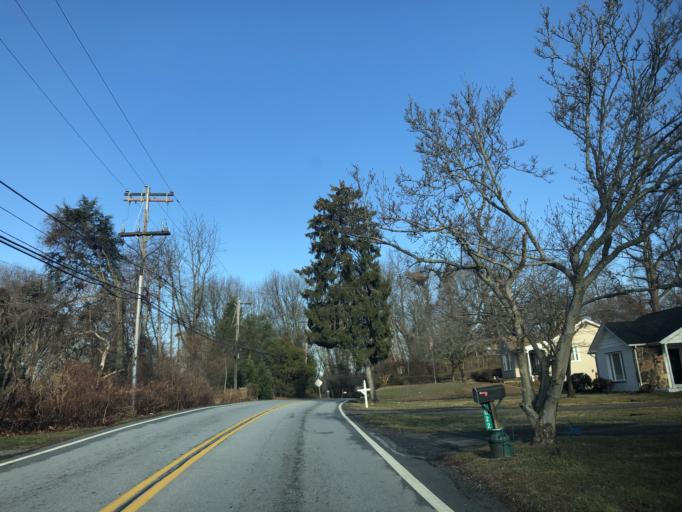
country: US
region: Pennsylvania
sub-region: Delaware County
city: Chester Heights
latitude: 39.8676
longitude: -75.4674
